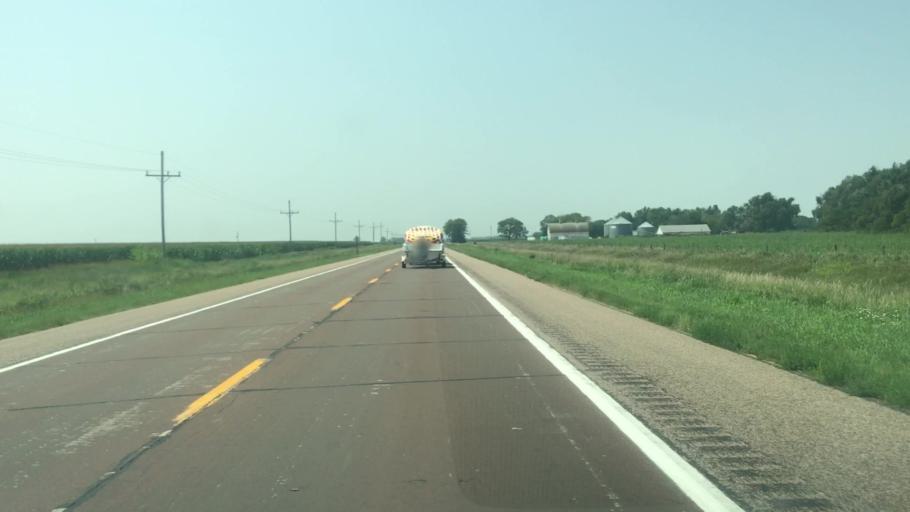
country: US
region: Nebraska
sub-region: Hall County
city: Grand Island
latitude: 40.9673
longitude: -98.4492
